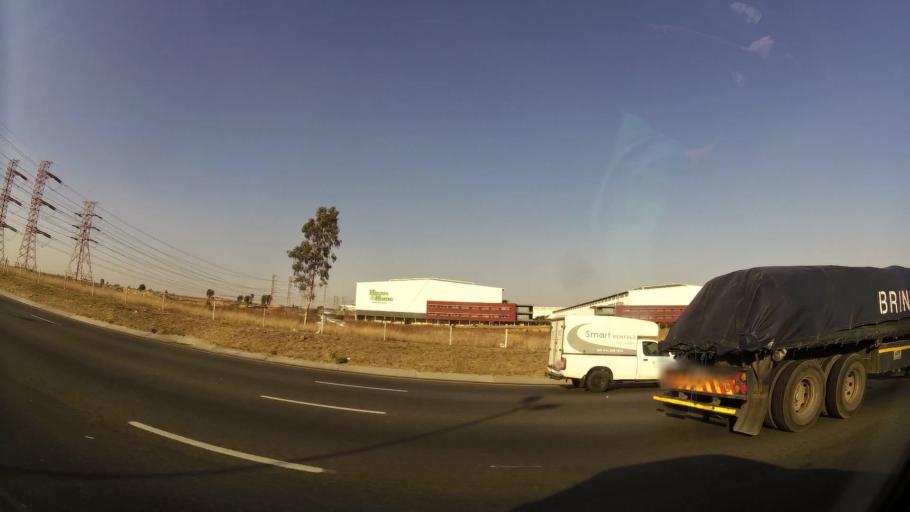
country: ZA
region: Gauteng
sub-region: Ekurhuleni Metropolitan Municipality
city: Germiston
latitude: -26.2297
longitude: 28.1260
